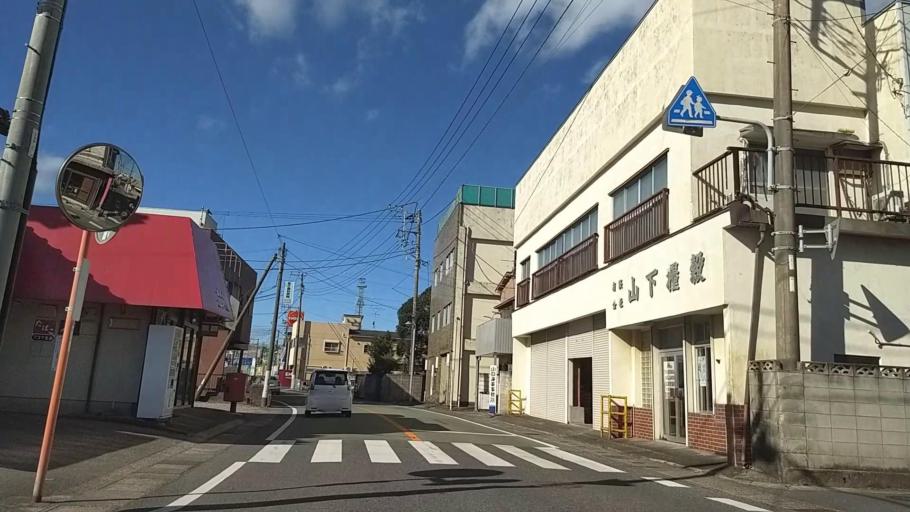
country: JP
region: Chiba
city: Tateyama
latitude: 34.9930
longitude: 139.8657
